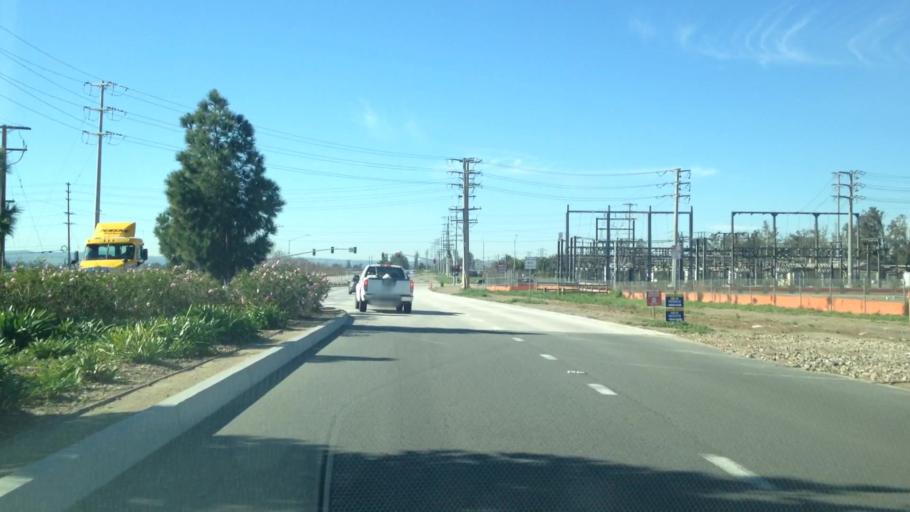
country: US
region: California
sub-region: Riverside County
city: Mira Loma
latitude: 33.9973
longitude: -117.5909
